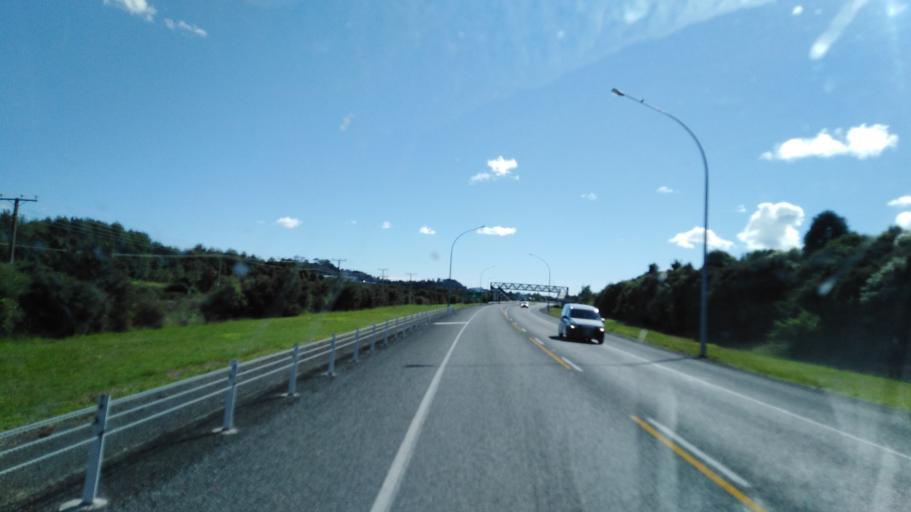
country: NZ
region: Bay of Plenty
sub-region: Tauranga City
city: Tauranga
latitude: -37.7422
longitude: 176.1055
